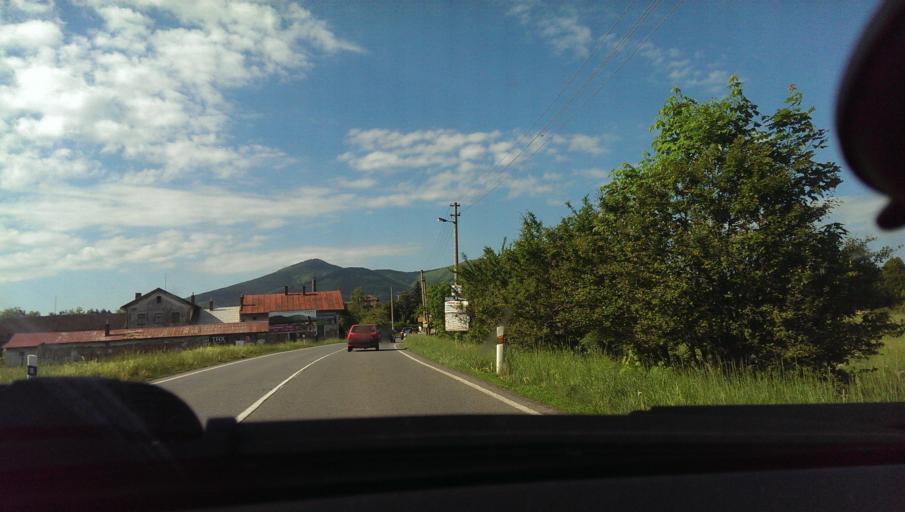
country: CZ
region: Moravskoslezsky
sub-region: Okres Frydek-Mistek
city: Celadna
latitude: 49.5512
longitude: 18.3404
